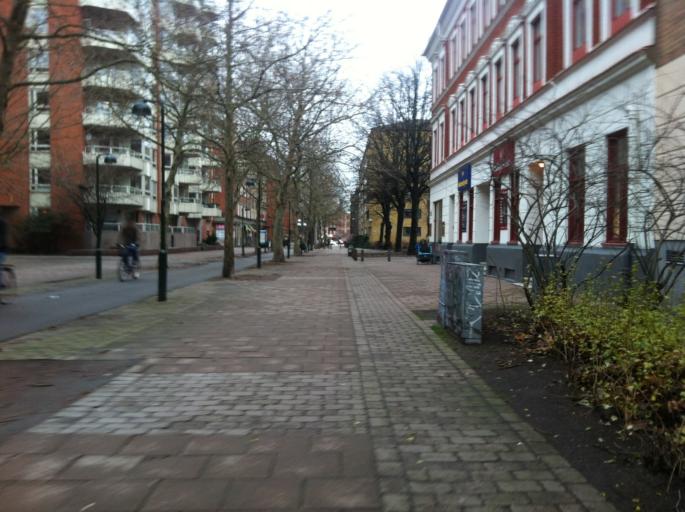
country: SE
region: Skane
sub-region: Malmo
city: Malmoe
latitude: 55.5984
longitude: 13.0066
